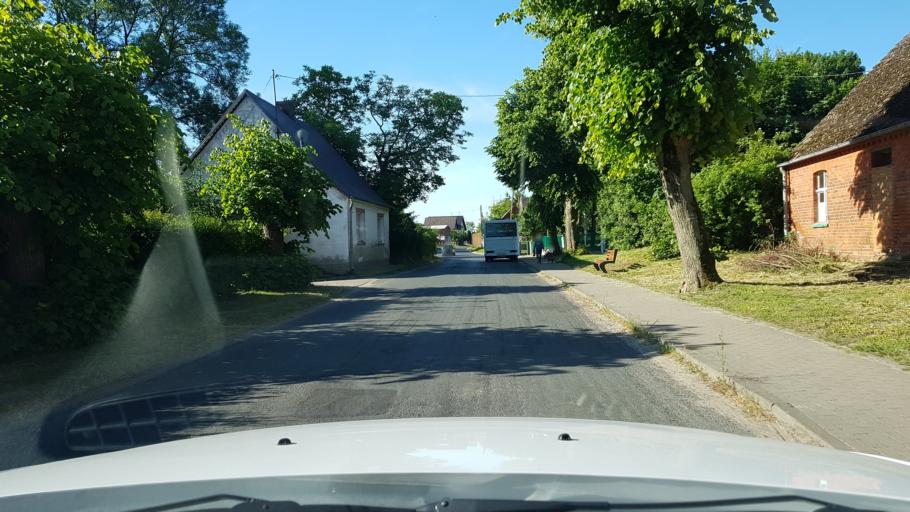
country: PL
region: West Pomeranian Voivodeship
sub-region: Powiat pyrzycki
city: Bielice
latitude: 53.2201
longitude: 14.6099
